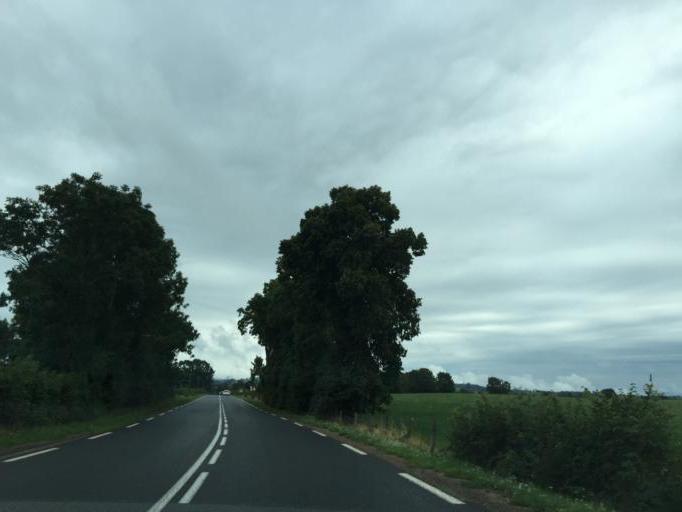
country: FR
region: Midi-Pyrenees
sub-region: Departement de l'Aveyron
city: Laguiole
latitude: 44.6211
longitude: 2.8156
